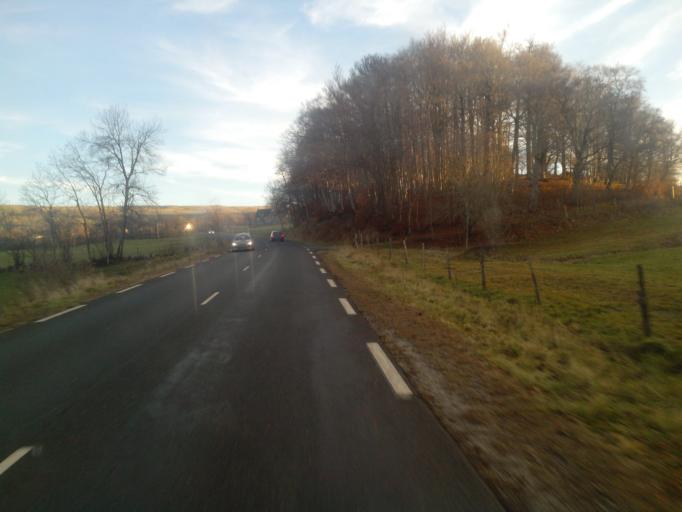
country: FR
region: Auvergne
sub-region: Departement du Cantal
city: Riom-es-Montagnes
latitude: 45.2441
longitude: 2.7188
